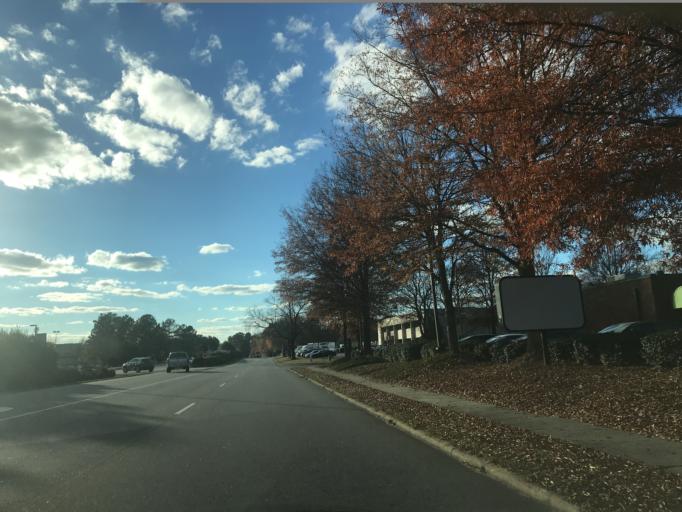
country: US
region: North Carolina
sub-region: Wake County
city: Raleigh
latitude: 35.8498
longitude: -78.5827
